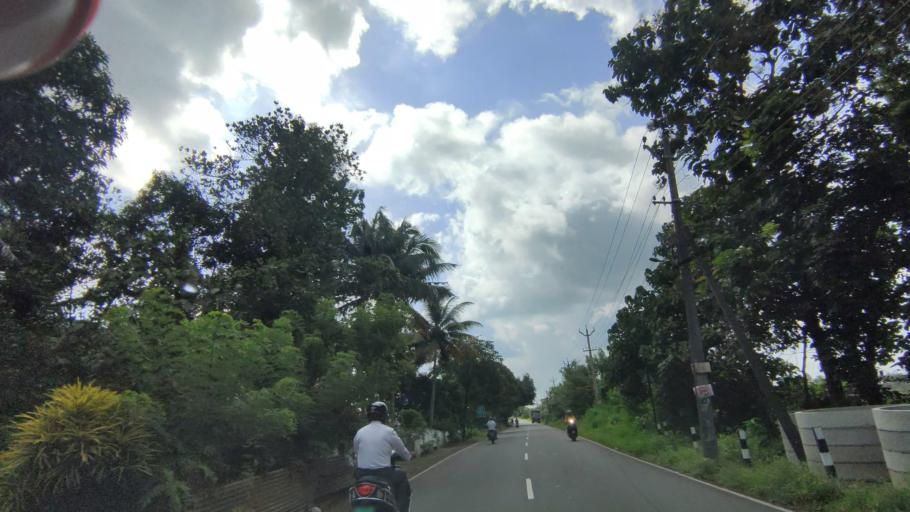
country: IN
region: Kerala
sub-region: Kottayam
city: Vaikam
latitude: 9.6943
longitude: 76.4885
